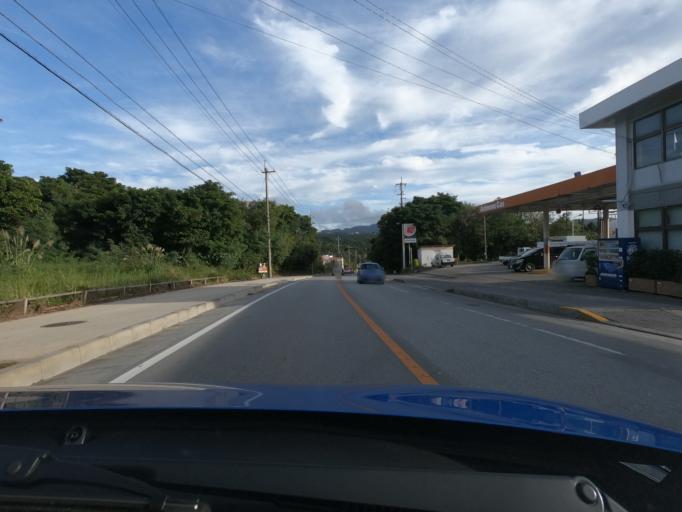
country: JP
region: Okinawa
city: Nago
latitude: 26.6807
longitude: 127.8862
